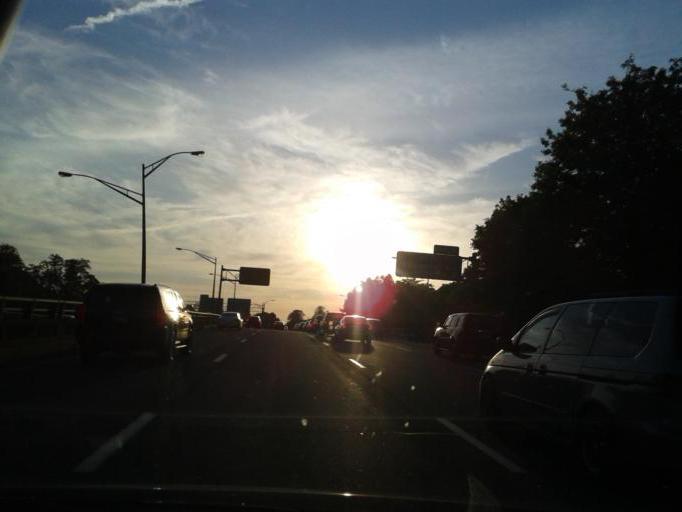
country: US
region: New York
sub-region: Westchester County
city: Bronxville
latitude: 40.9229
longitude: -73.8216
